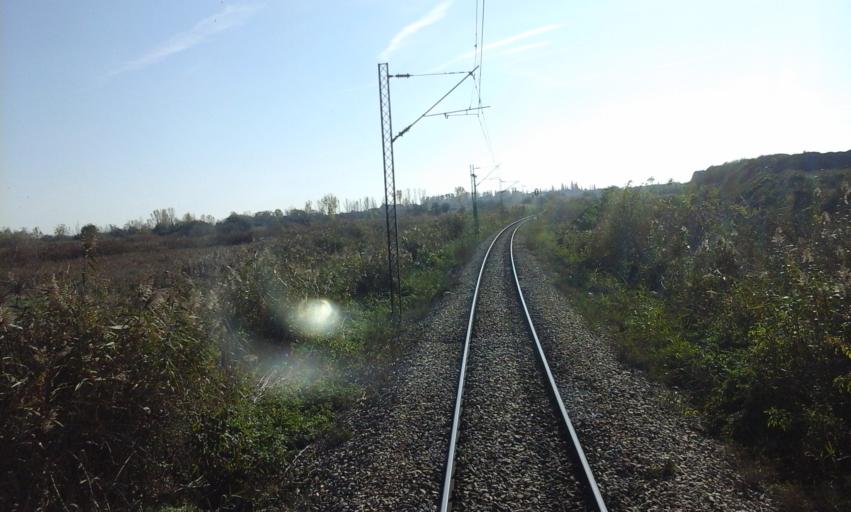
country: RS
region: Autonomna Pokrajina Vojvodina
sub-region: Severnobacki Okrug
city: Subotica
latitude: 46.0824
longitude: 19.6899
